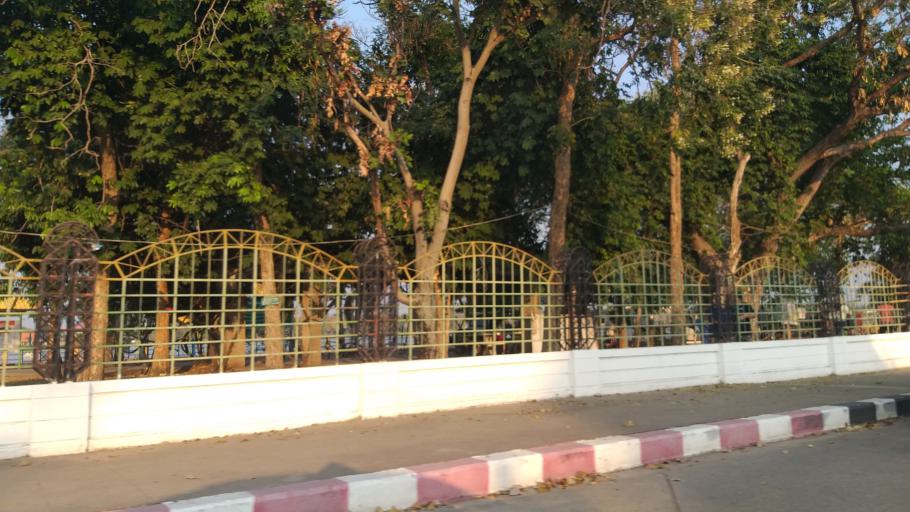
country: TH
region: Khon Kaen
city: Khon Kaen
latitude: 16.4147
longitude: 102.8353
